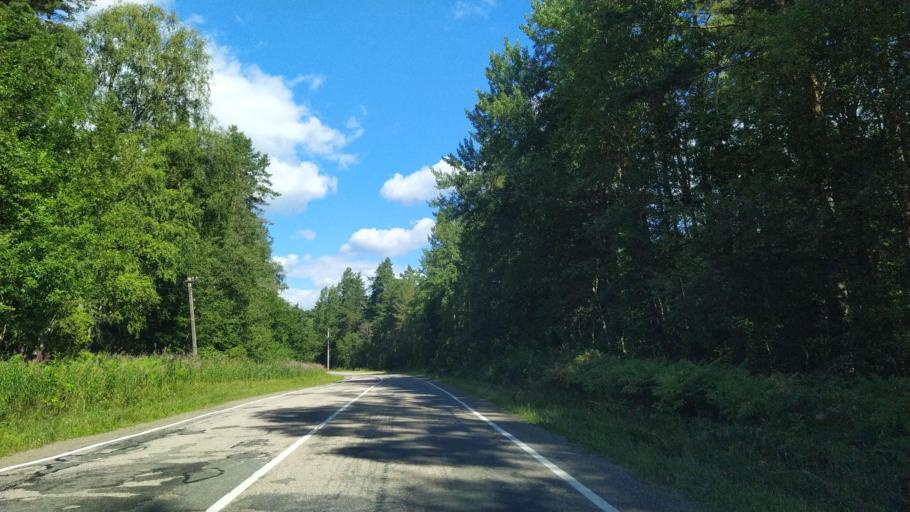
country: RU
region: Leningrad
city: Priozersk
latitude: 60.9726
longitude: 30.2820
